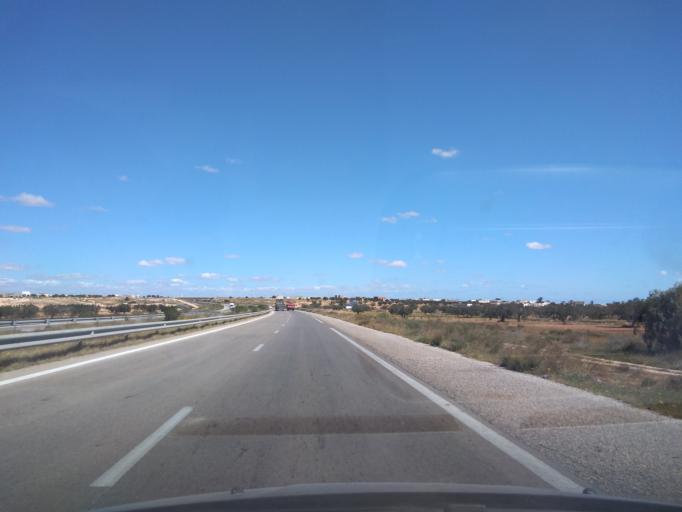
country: TN
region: Safaqis
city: Jabinyanah
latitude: 34.9552
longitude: 10.7378
